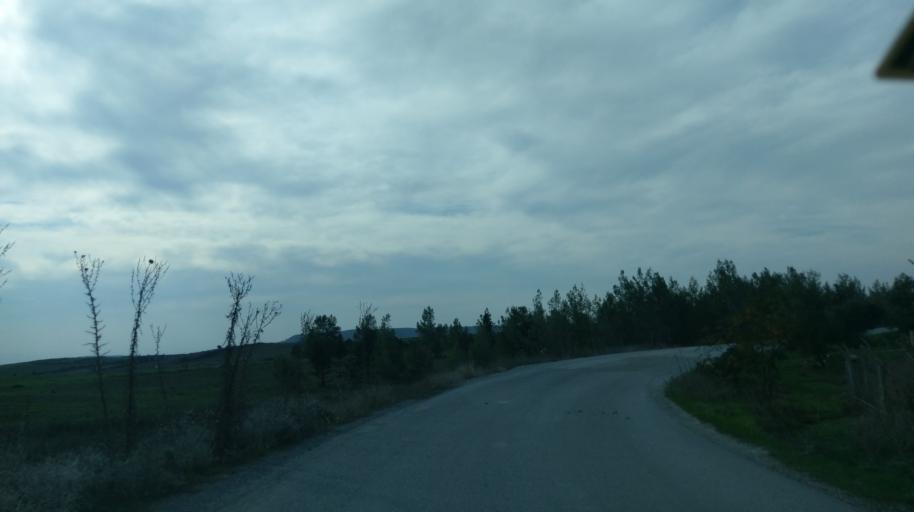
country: CY
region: Keryneia
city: Lapithos
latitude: 35.2865
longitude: 33.1259
